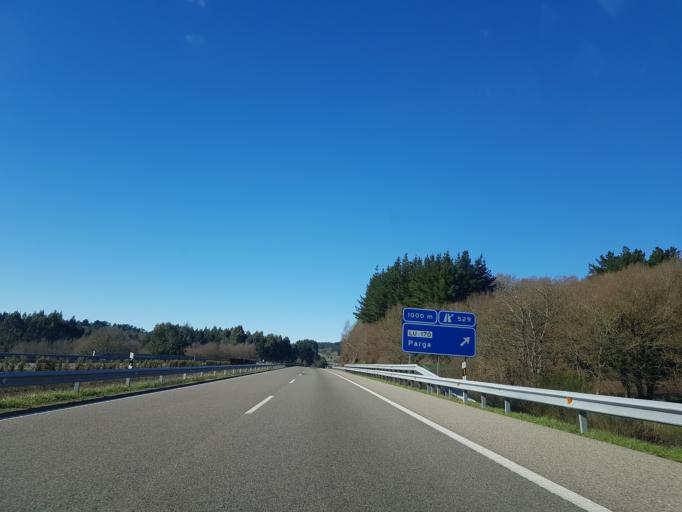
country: ES
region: Galicia
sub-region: Provincia de Lugo
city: Guitiriz
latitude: 43.1789
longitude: -7.8060
